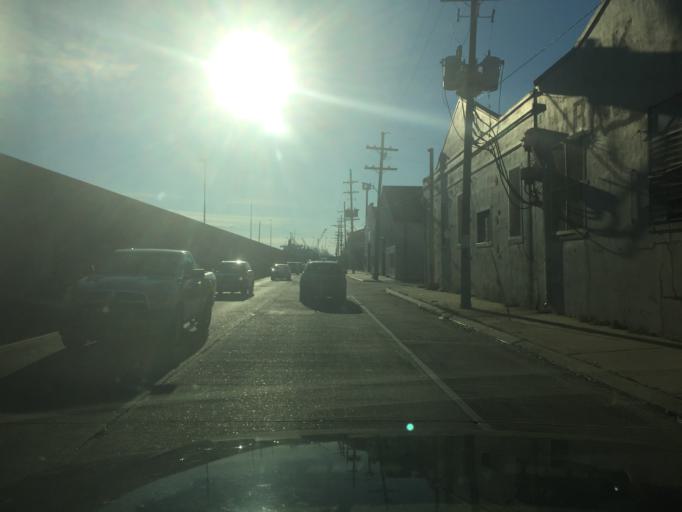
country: US
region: Louisiana
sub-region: Jefferson Parish
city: Gretna
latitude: 29.9230
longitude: -90.0720
